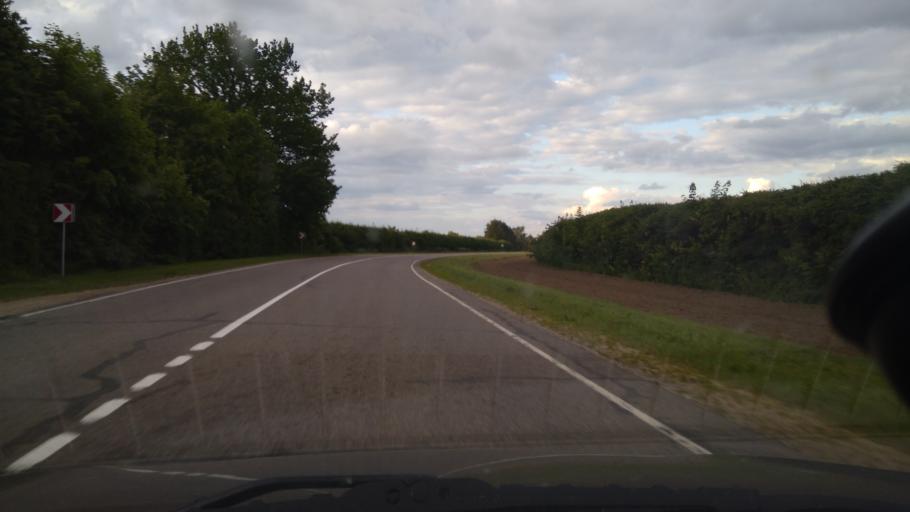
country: BY
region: Grodnenskaya
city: Shchuchin
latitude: 53.5110
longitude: 24.6874
